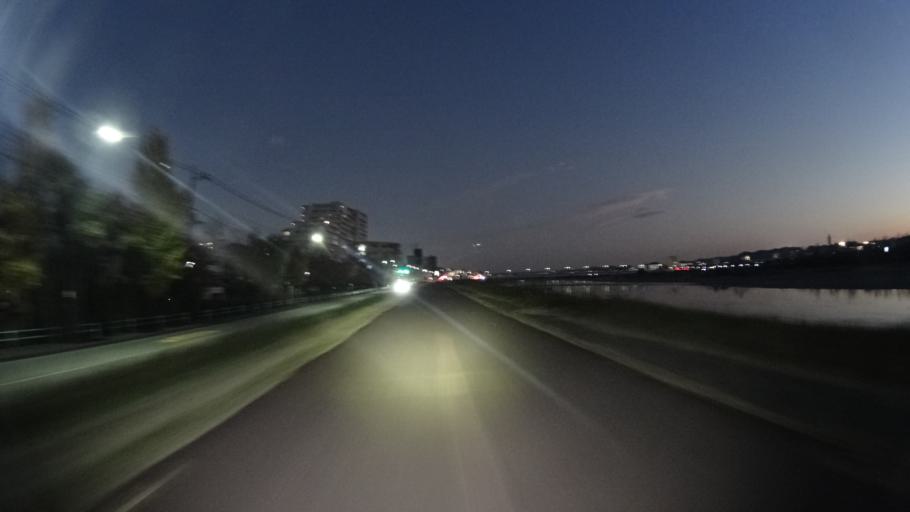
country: JP
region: Tokyo
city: Chofugaoka
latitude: 35.6508
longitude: 139.5193
